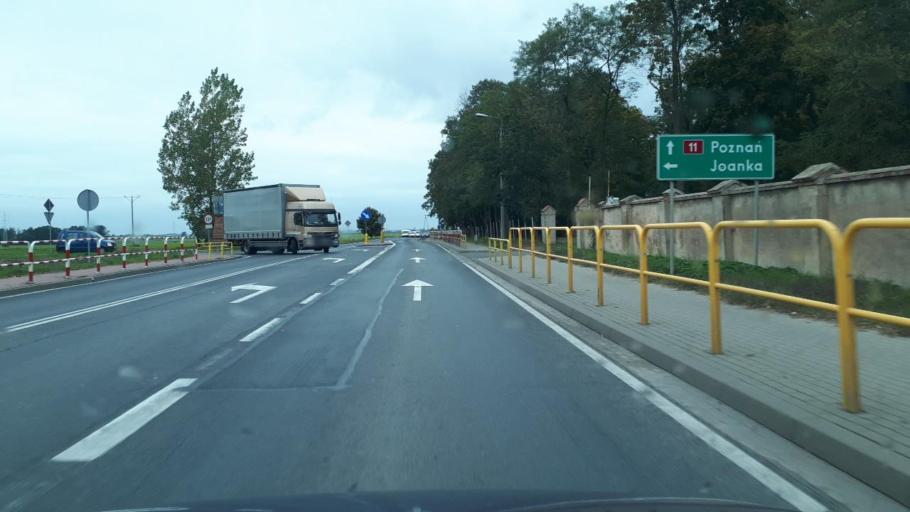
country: PL
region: Greater Poland Voivodeship
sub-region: Powiat kepinski
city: Slupia pod Kepnem
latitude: 51.2396
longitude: 18.0375
